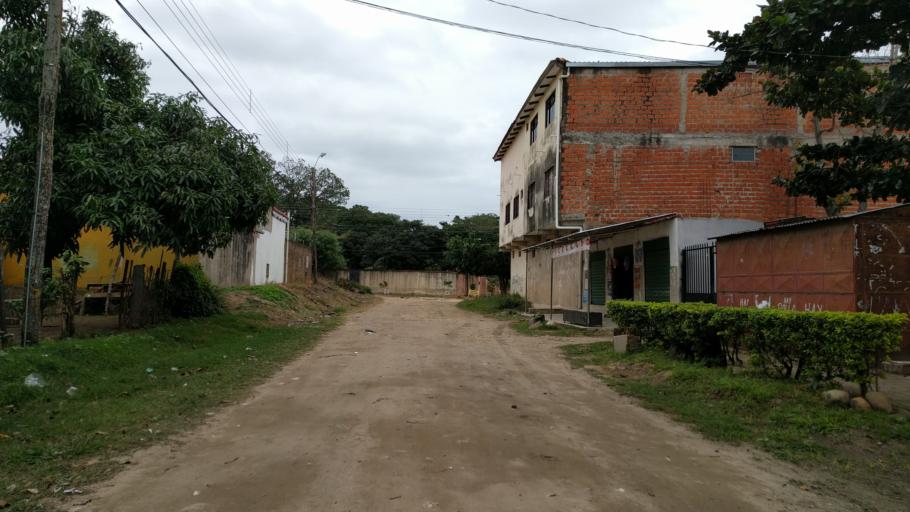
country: BO
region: Santa Cruz
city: Santa Cruz de la Sierra
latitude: -17.8072
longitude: -63.2183
